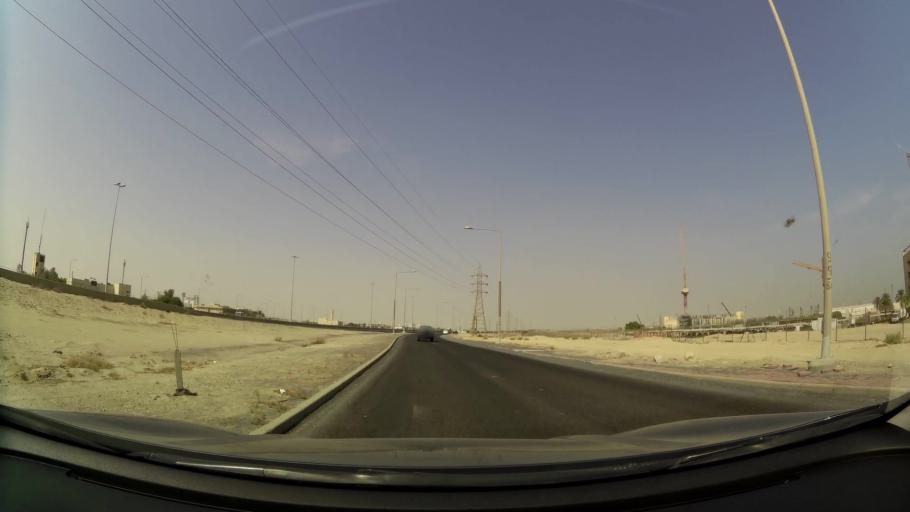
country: KW
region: Al Ahmadi
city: Al Fahahil
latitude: 28.9996
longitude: 48.1410
